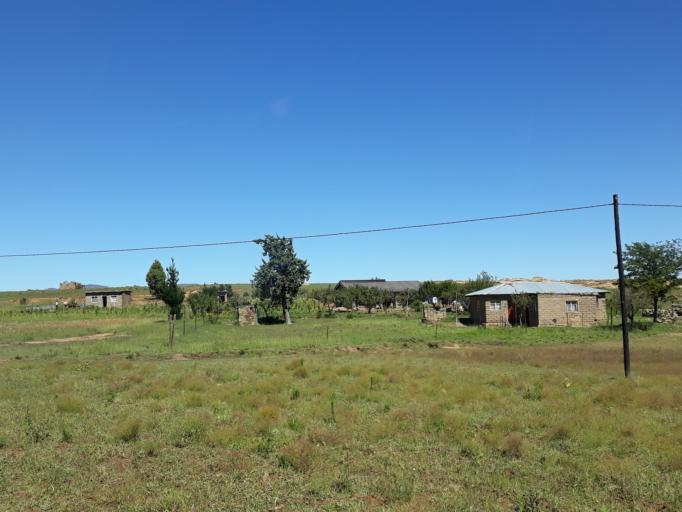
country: LS
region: Quthing
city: Quthing
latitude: -30.3371
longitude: 27.5299
